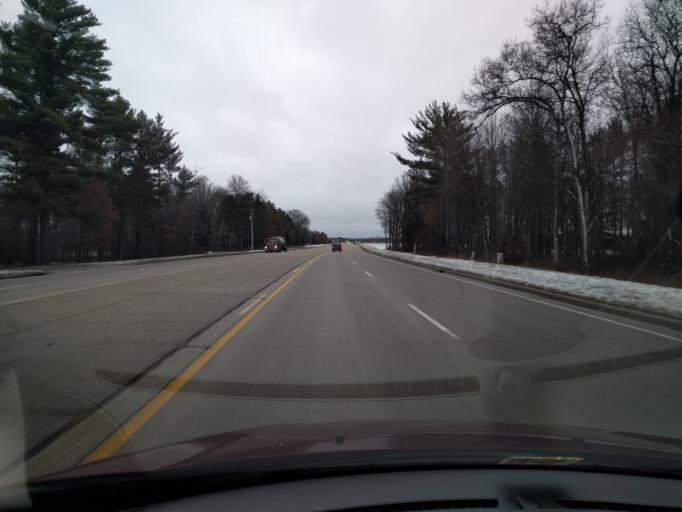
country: US
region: Wisconsin
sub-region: Portage County
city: Whiting
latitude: 44.5236
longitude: -89.4908
